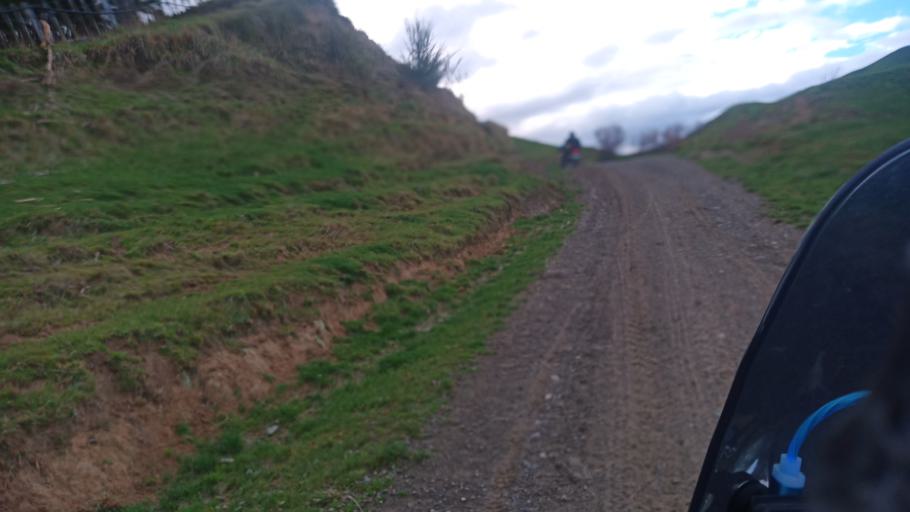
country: NZ
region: Gisborne
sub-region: Gisborne District
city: Gisborne
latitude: -38.3441
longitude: 177.9155
